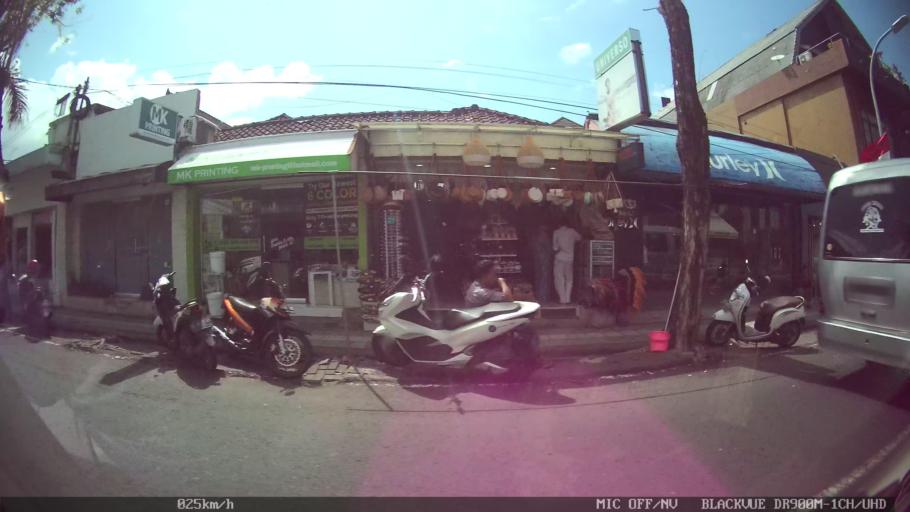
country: ID
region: Bali
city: Kuta
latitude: -8.6959
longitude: 115.1686
